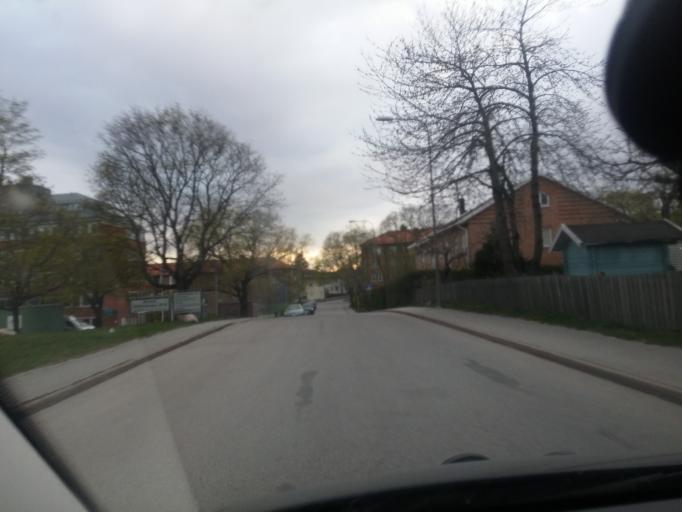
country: SE
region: Stockholm
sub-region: Sundbybergs Kommun
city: Sundbyberg
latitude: 59.3583
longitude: 17.9550
